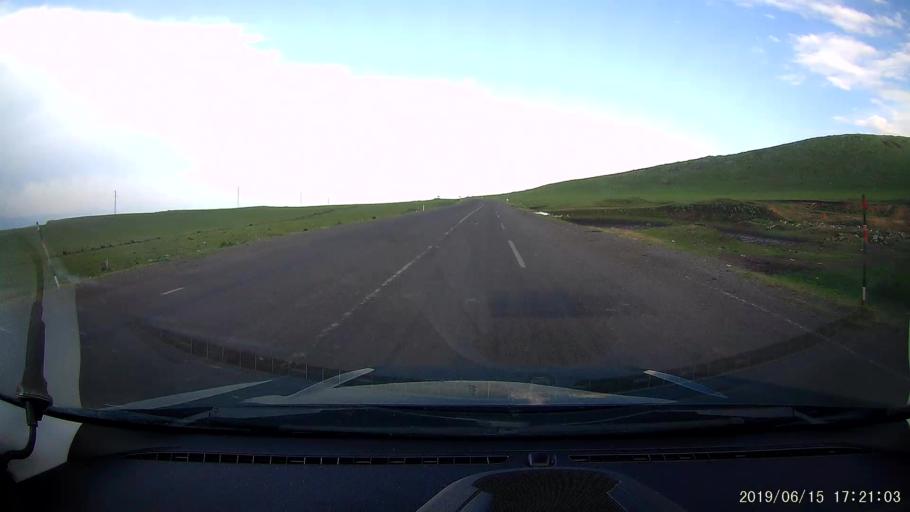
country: TR
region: Kars
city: Basgedikler
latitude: 40.6172
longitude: 43.3166
